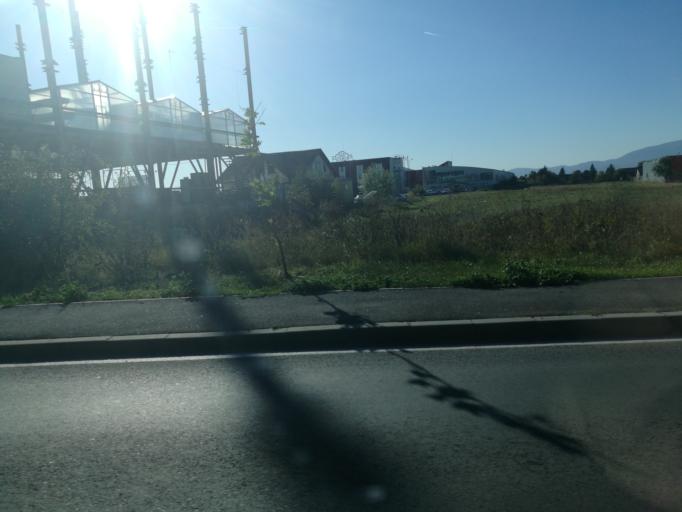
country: RO
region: Brasov
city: Brasov
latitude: 45.6739
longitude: 25.5894
